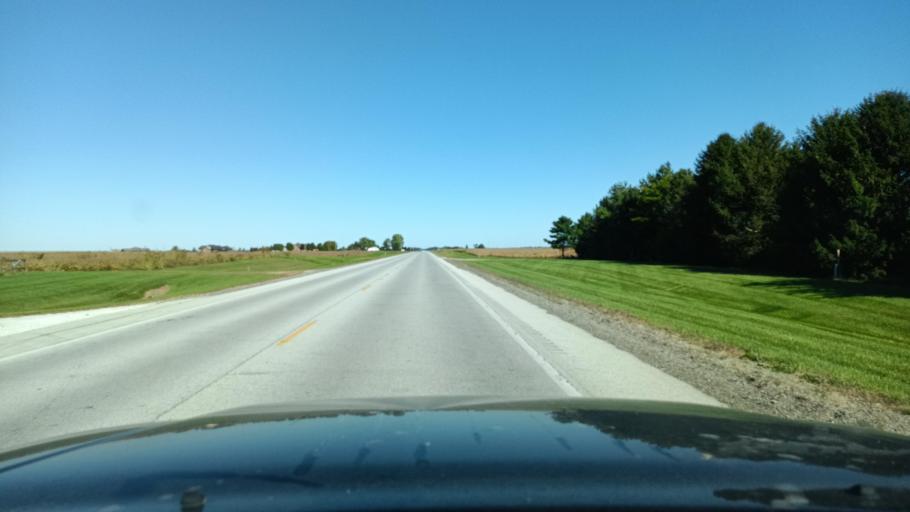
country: US
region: Illinois
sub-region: Champaign County
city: Philo
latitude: 40.0340
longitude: -88.1616
